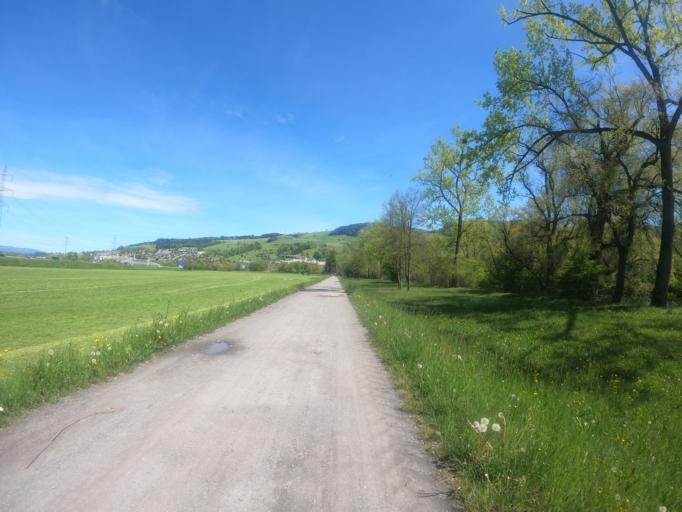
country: CH
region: Lucerne
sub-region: Lucerne-Land District
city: Root
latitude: 47.1181
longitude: 8.3787
